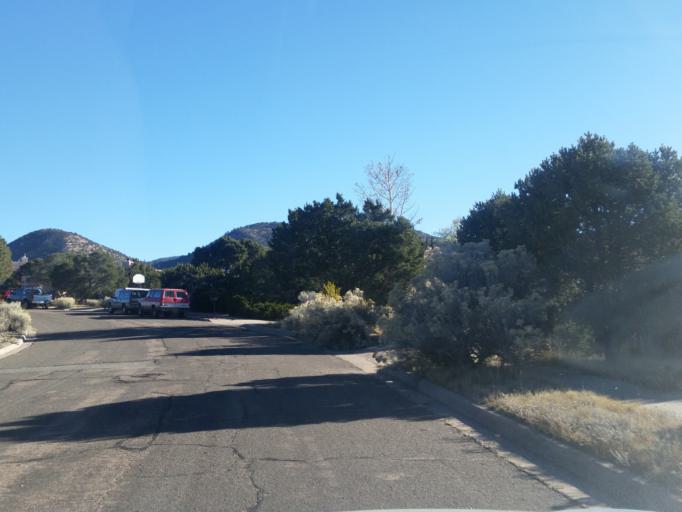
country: US
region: New Mexico
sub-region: Santa Fe County
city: Santa Fe
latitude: 35.6467
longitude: -105.9299
